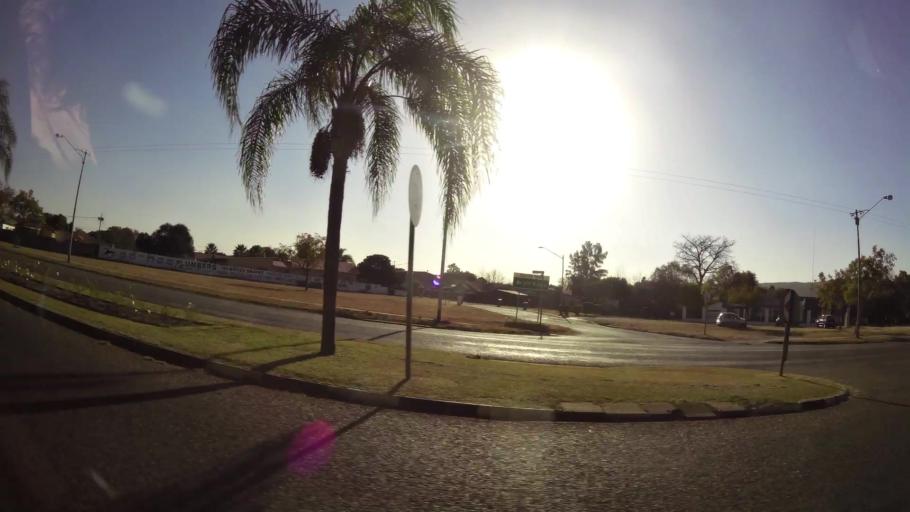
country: ZA
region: Gauteng
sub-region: City of Tshwane Metropolitan Municipality
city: Pretoria
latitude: -25.7143
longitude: 28.2226
